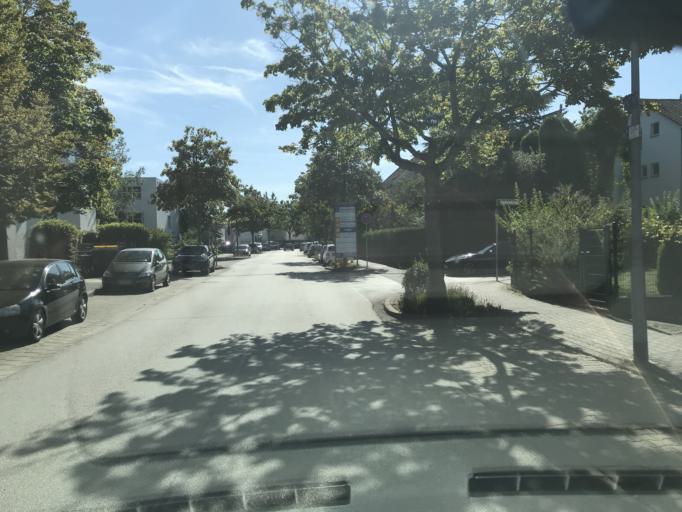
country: DE
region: Hesse
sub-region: Regierungsbezirk Darmstadt
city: Wiesbaden
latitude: 50.0562
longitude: 8.2950
